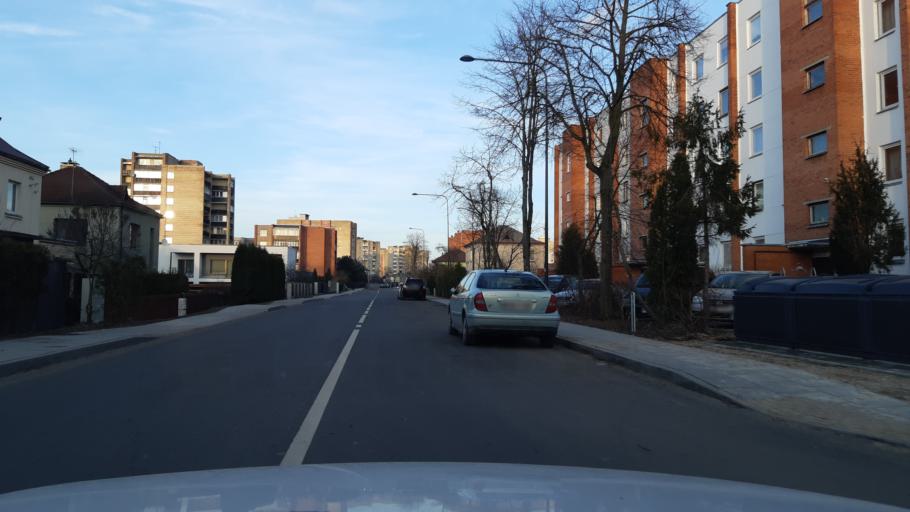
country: LT
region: Kauno apskritis
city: Dainava (Kaunas)
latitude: 54.8883
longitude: 23.9417
